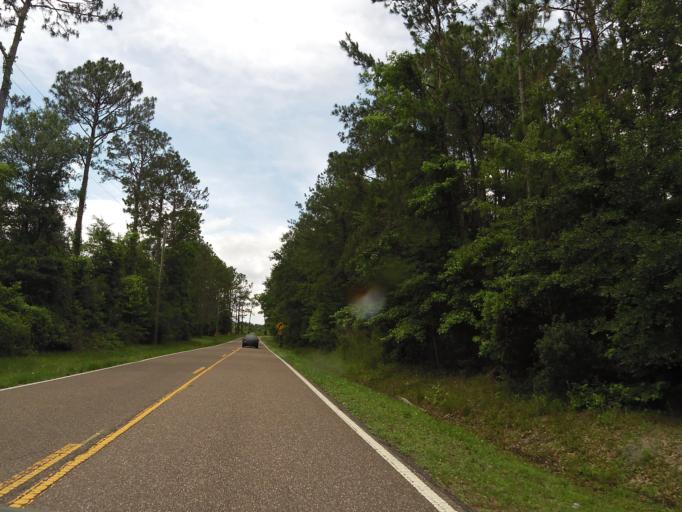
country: US
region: Florida
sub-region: Nassau County
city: Nassau Village-Ratliff
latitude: 30.5190
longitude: -81.7477
